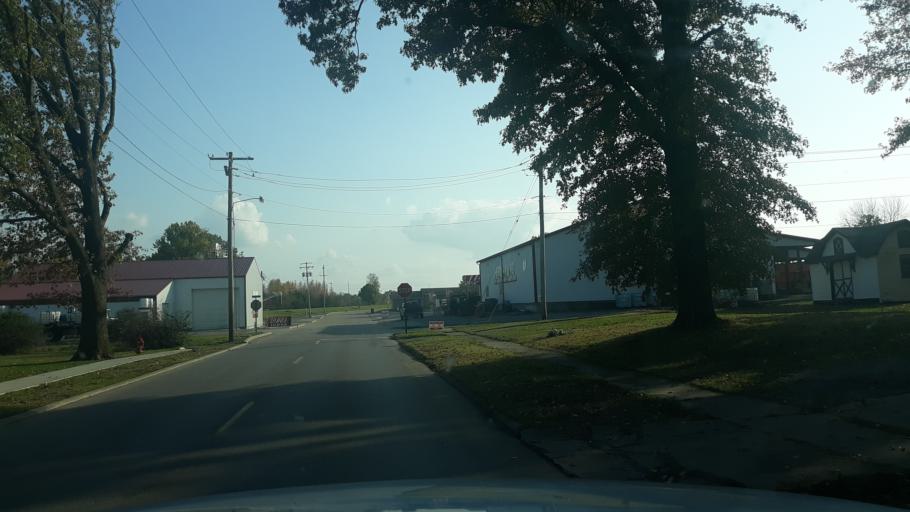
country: US
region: Illinois
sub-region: Saline County
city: Harrisburg
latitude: 37.7244
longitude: -88.5403
